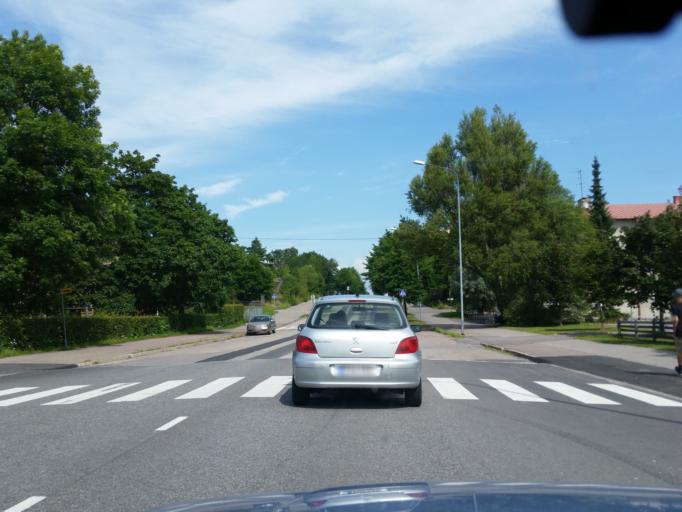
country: FI
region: Uusimaa
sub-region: Raaseporin
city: Hanko
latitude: 59.8291
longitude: 22.9660
